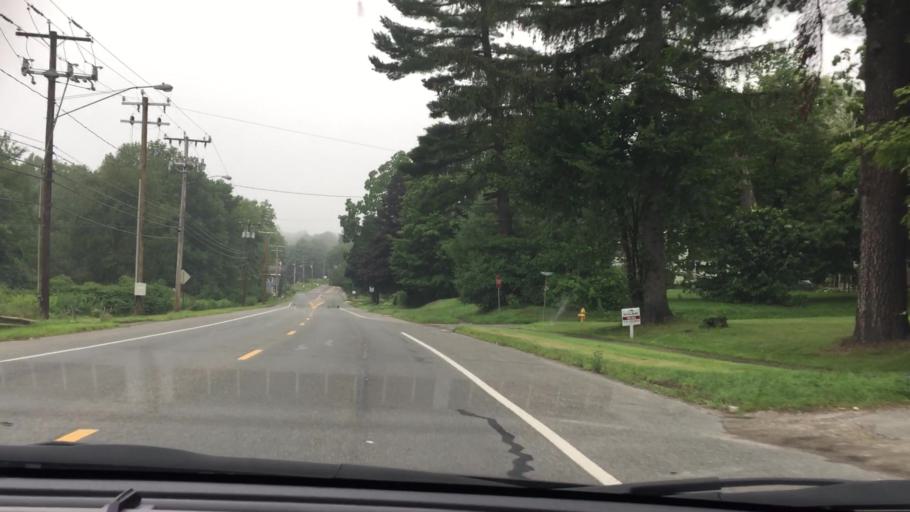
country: US
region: Massachusetts
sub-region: Berkshire County
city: Pittsfield
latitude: 42.4404
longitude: -73.2912
